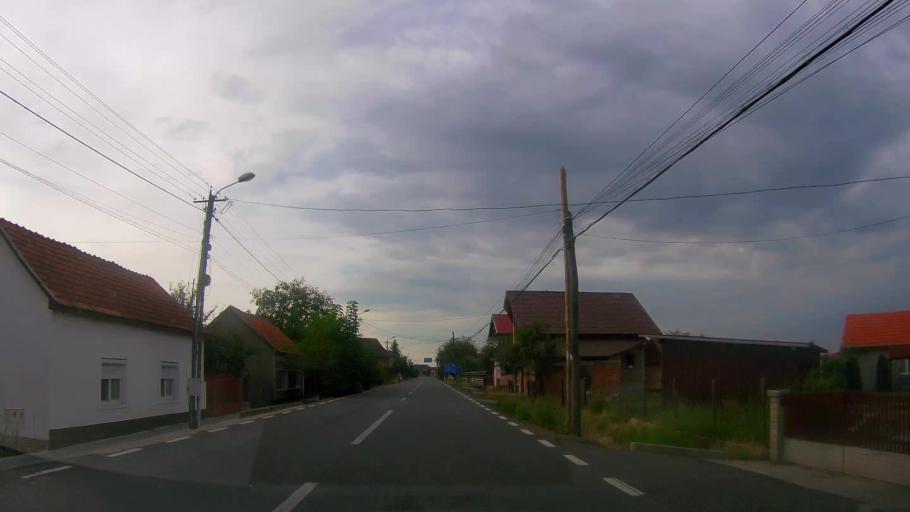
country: RO
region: Satu Mare
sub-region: Comuna Halmeu
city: Halmeu
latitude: 47.9811
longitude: 23.0089
